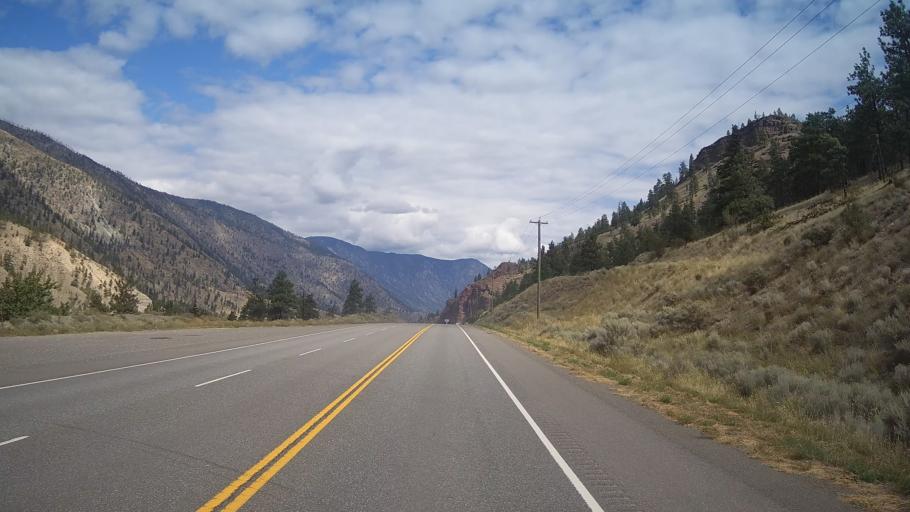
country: CA
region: British Columbia
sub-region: Thompson-Nicola Regional District
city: Ashcroft
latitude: 50.2978
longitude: -121.3921
